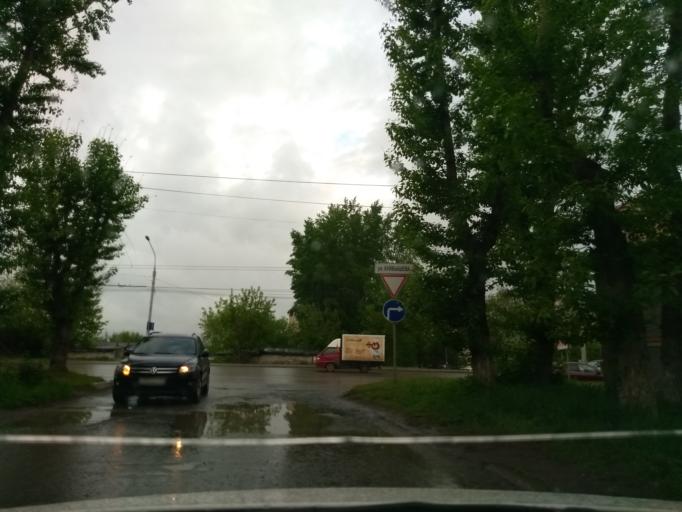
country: RU
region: Perm
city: Perm
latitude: 57.9831
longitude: 56.2471
